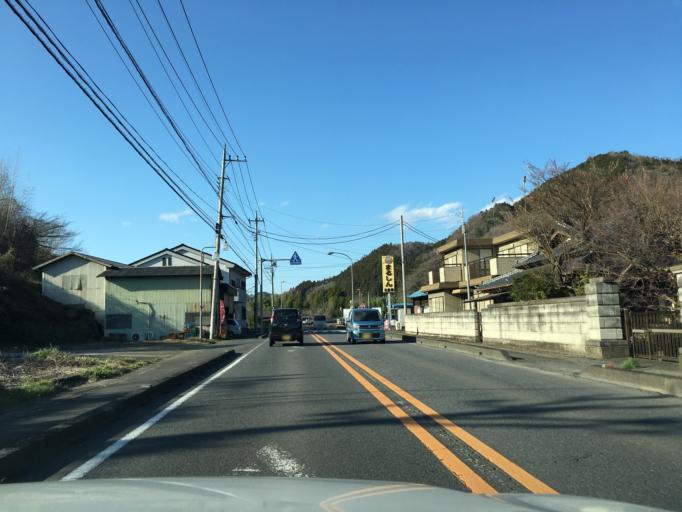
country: JP
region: Ibaraki
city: Omiya
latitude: 36.6538
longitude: 140.3932
